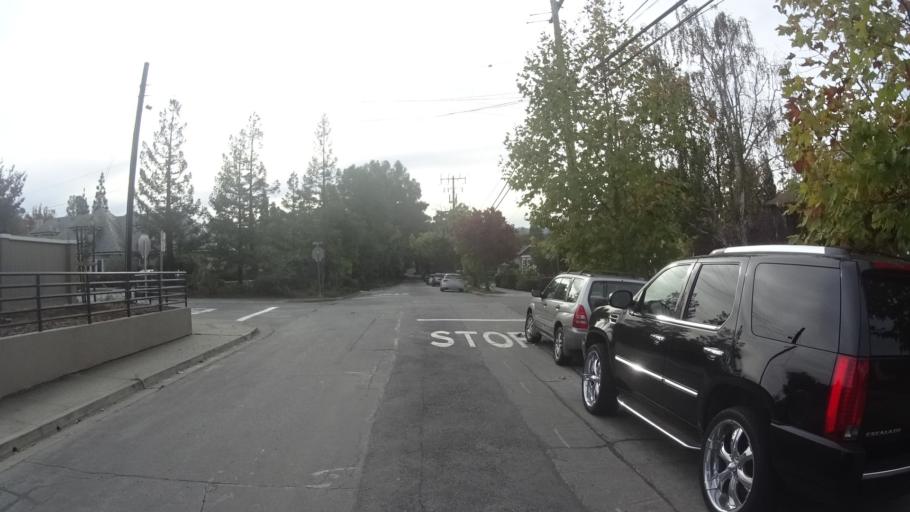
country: US
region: California
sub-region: San Mateo County
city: Burlingame
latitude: 37.5808
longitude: -122.3634
